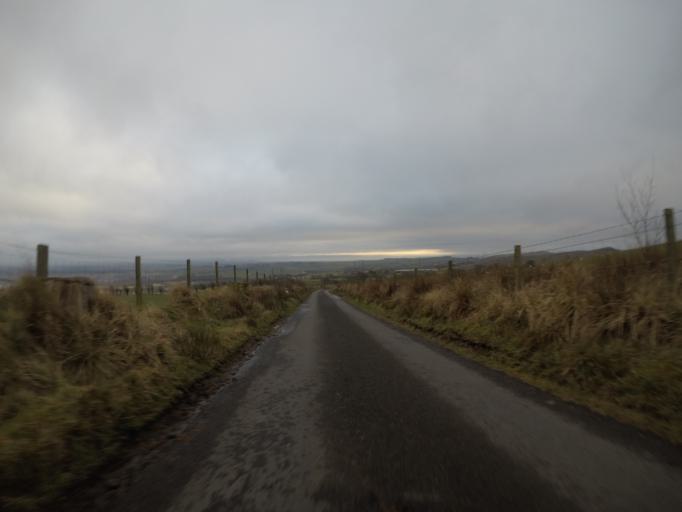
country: GB
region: Scotland
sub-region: North Ayrshire
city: Dalry
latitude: 55.7282
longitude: -4.7639
